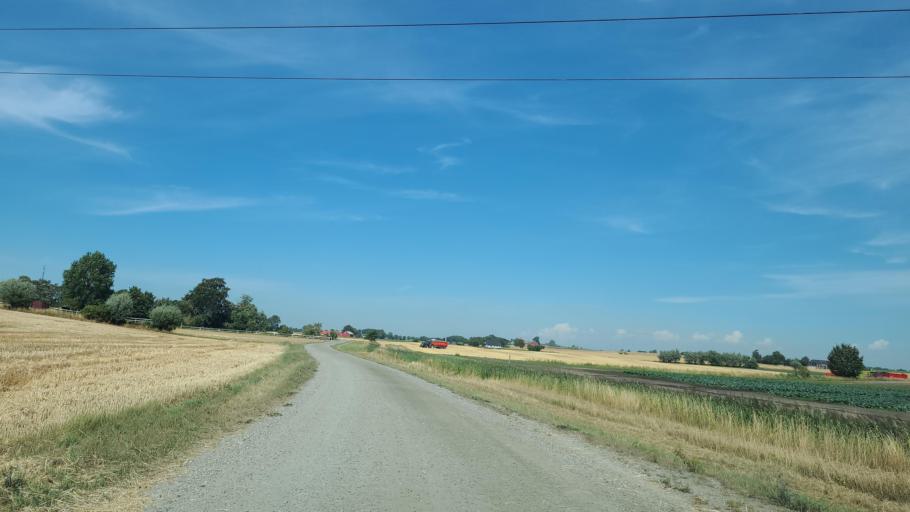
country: SE
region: Skane
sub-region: Trelleborgs Kommun
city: Skare
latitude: 55.4184
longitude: 13.0659
